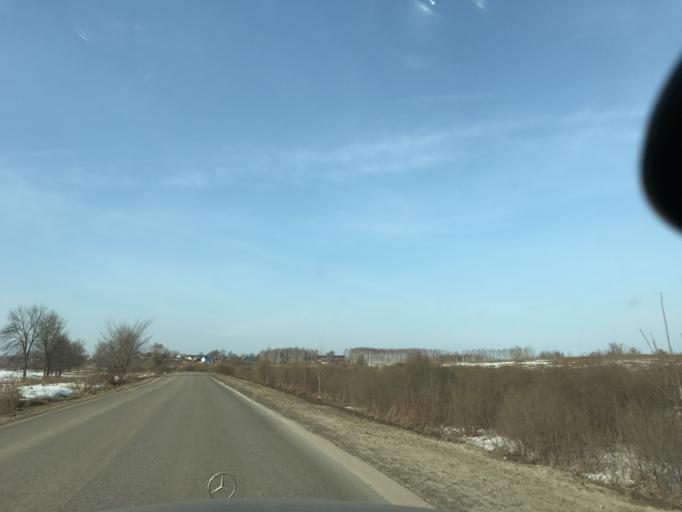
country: RU
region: Nizjnij Novgorod
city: Pavlovo
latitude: 55.9843
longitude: 43.0470
